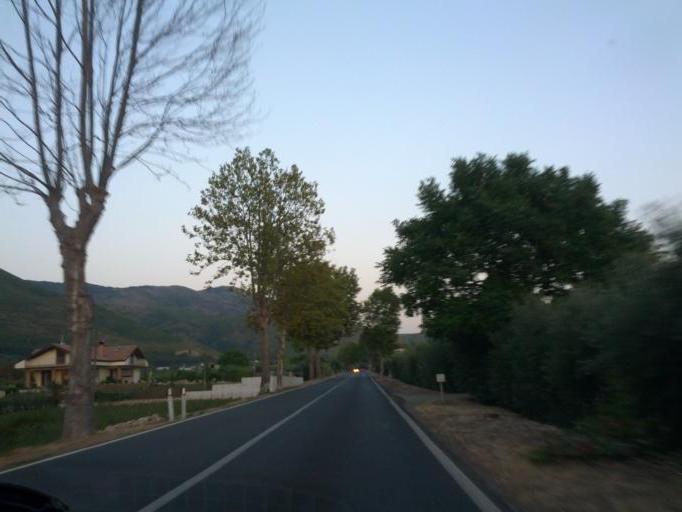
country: IT
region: Latium
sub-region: Provincia di Latina
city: Fondi
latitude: 41.3323
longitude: 13.4645
